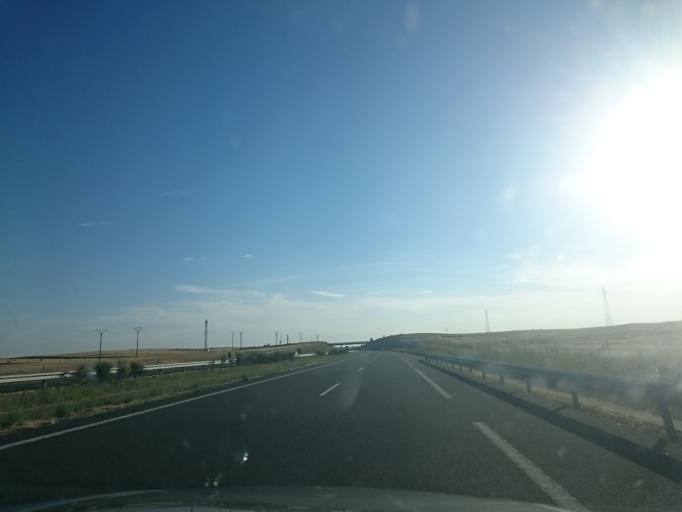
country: ES
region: Castille and Leon
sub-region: Provincia de Palencia
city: San Mames de Campos
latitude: 42.3689
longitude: -4.5411
